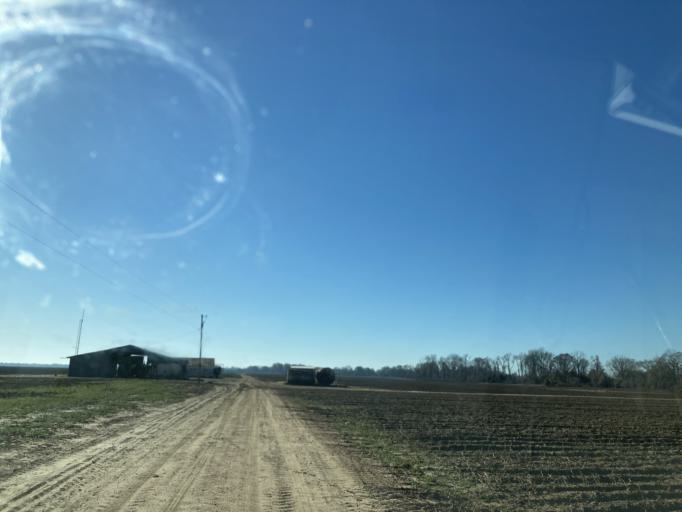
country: US
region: Mississippi
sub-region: Sharkey County
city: Rolling Fork
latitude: 32.8677
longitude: -90.6926
